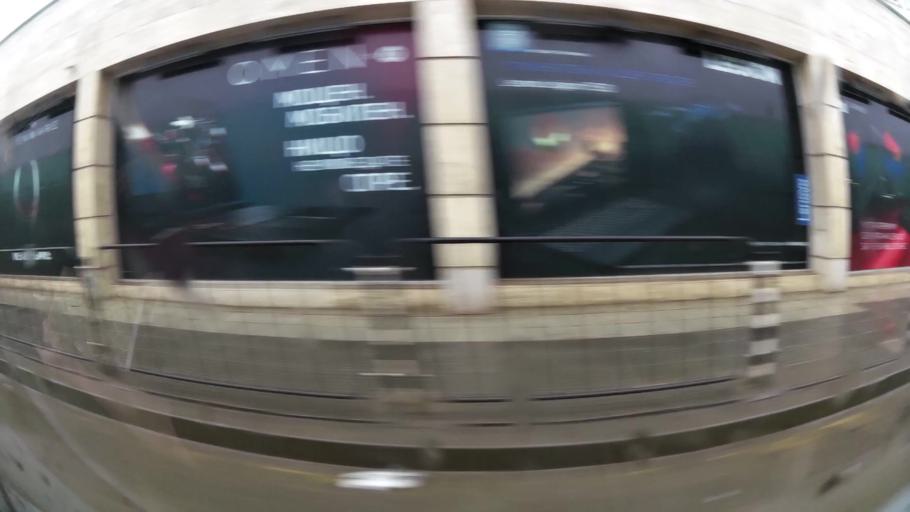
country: BG
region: Sofia-Capital
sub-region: Stolichna Obshtina
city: Sofia
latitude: 42.6592
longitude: 23.3631
